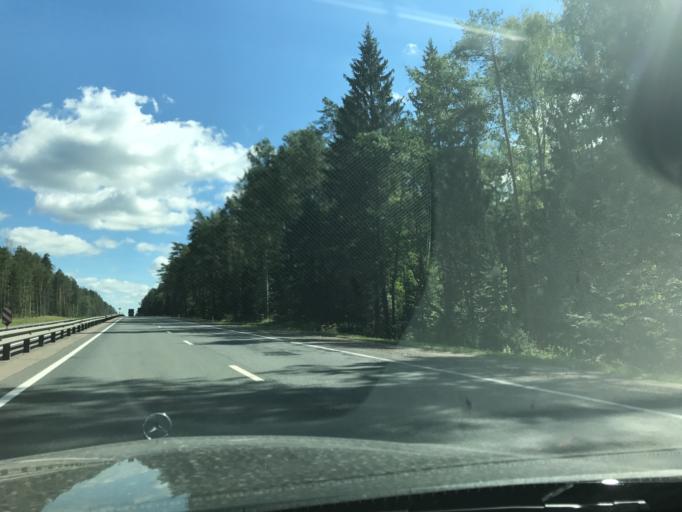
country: RU
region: Vladimir
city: Kameshkovo
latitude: 56.1977
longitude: 41.0218
